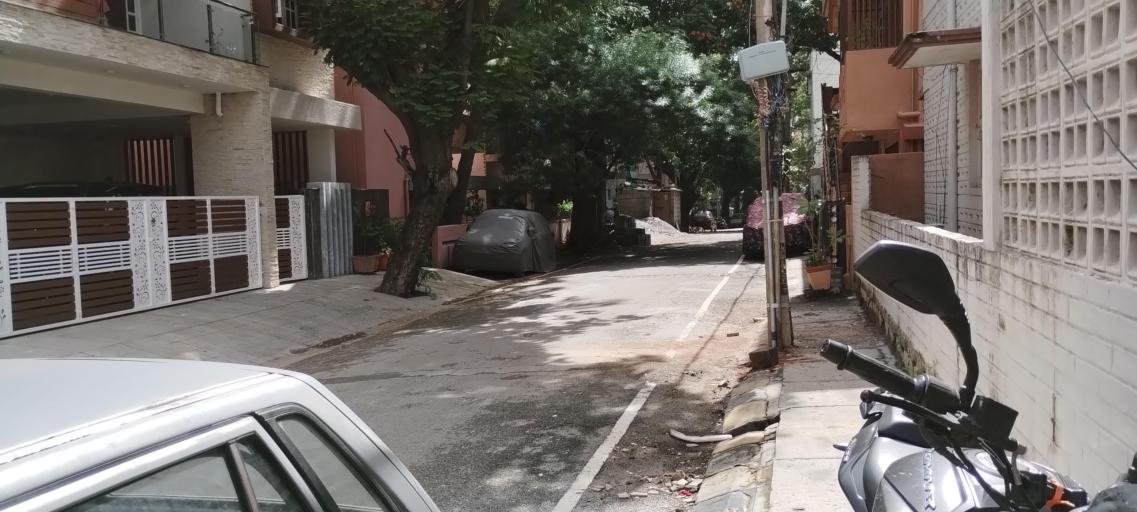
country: IN
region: Karnataka
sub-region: Bangalore Urban
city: Bangalore
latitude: 12.9423
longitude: 77.5396
